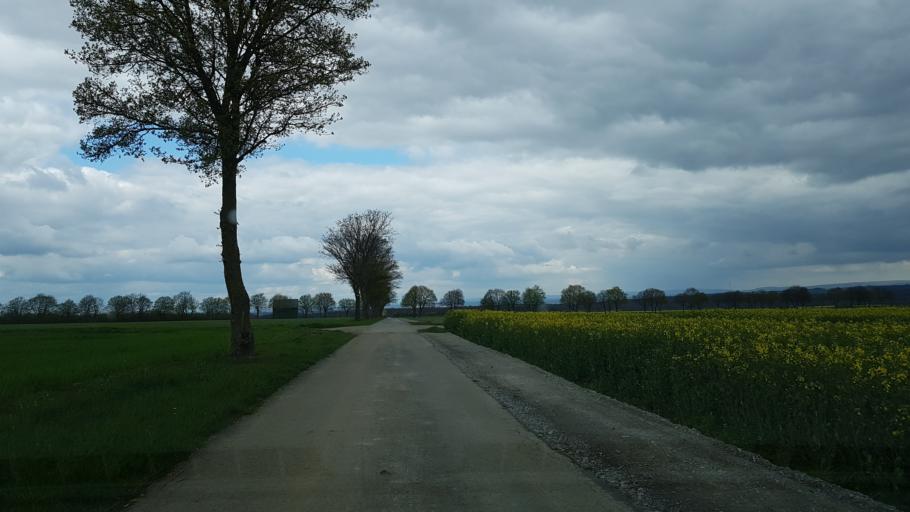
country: DE
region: North Rhine-Westphalia
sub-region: Regierungsbezirk Detmold
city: Wunnenberg
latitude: 51.6143
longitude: 8.7423
